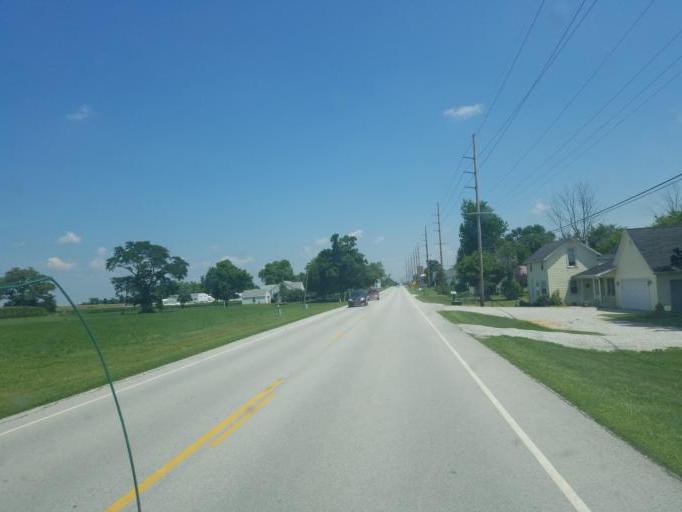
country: US
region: Ohio
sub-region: Auglaize County
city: Saint Marys
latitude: 40.5554
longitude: -84.3036
